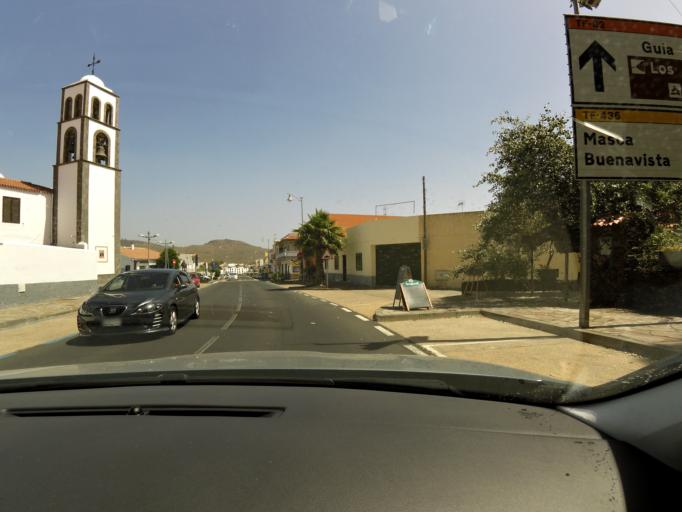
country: ES
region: Canary Islands
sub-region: Provincia de Santa Cruz de Tenerife
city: Santiago del Teide
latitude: 28.2978
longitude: -16.8163
